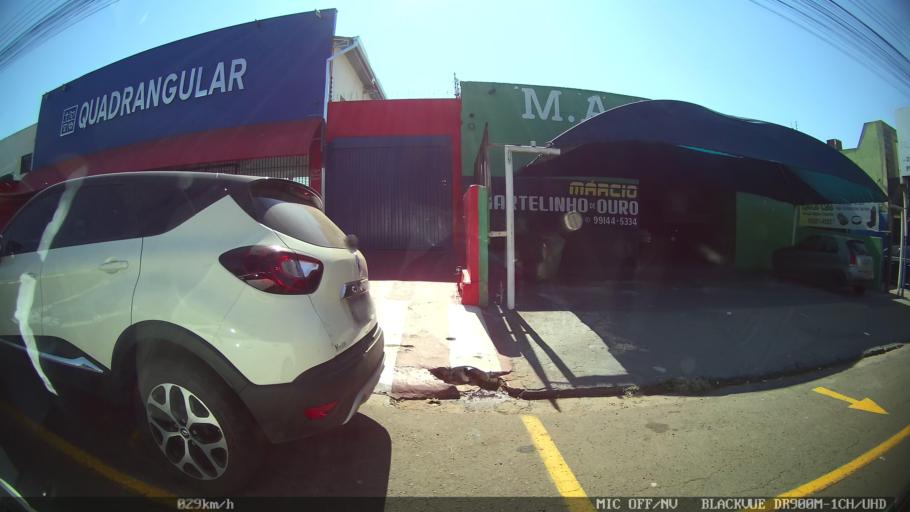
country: BR
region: Sao Paulo
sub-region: Sao Jose Do Rio Preto
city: Sao Jose do Rio Preto
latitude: -20.7775
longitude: -49.4047
